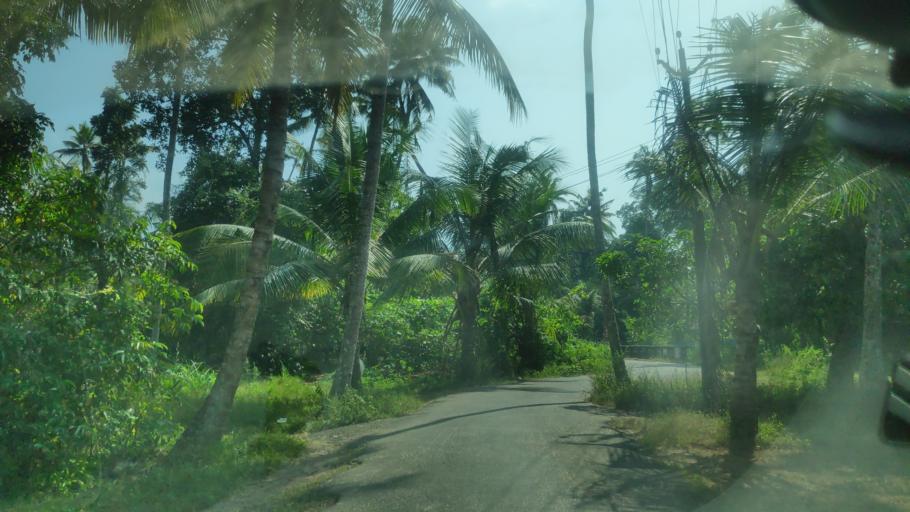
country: IN
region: Kerala
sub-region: Alappuzha
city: Vayalar
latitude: 9.6613
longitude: 76.3048
